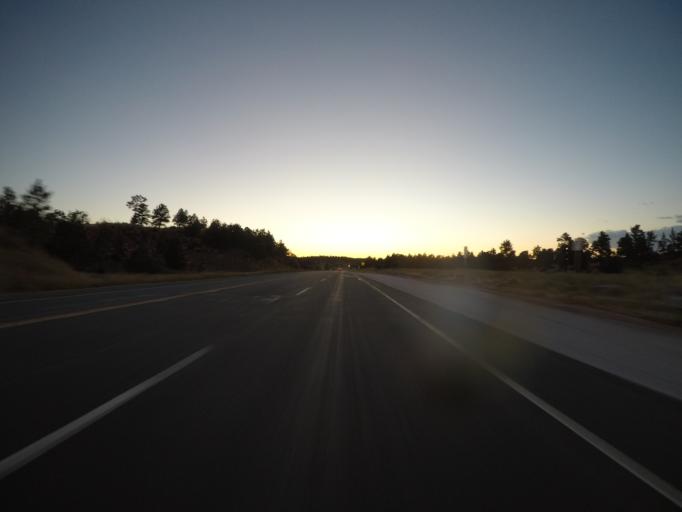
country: US
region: Wyoming
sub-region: Albany County
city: Laramie
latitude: 40.9843
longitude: -105.3998
